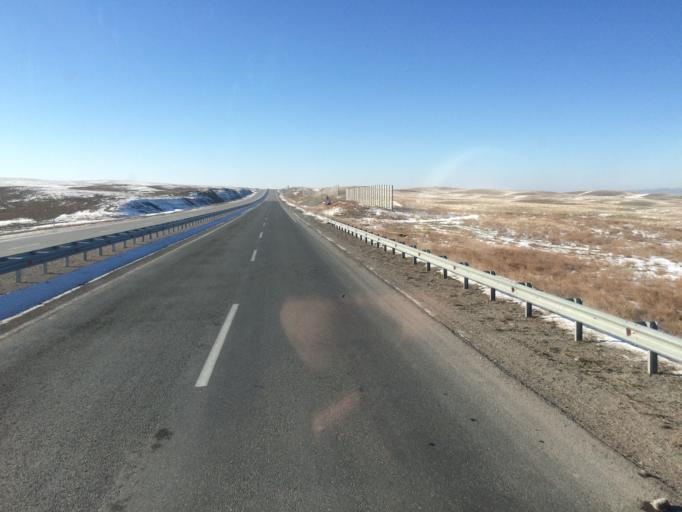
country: KZ
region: Zhambyl
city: Georgiyevka
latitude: 43.3638
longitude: 74.6992
